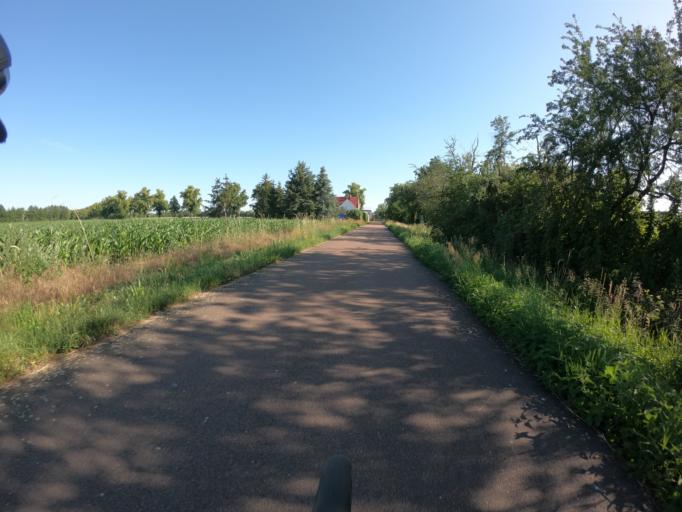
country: DE
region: Brandenburg
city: Juterbog
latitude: 52.0309
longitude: 13.0894
